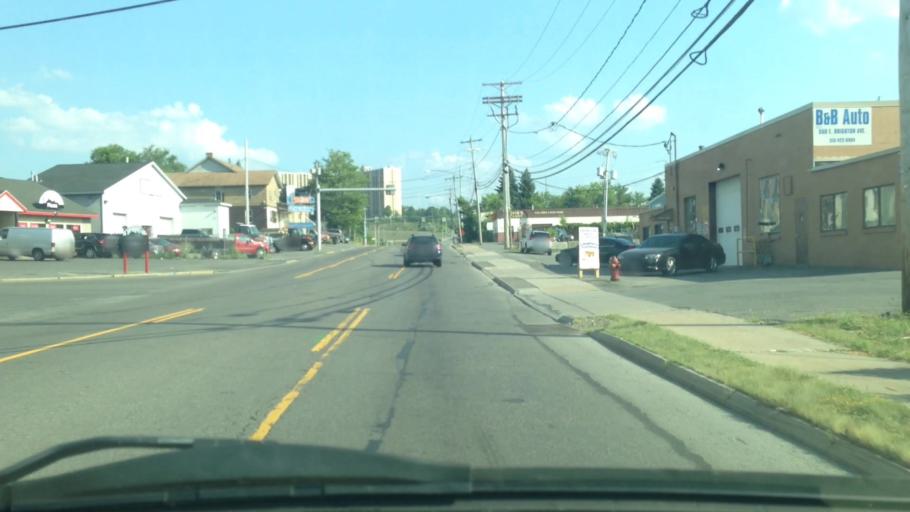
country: US
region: New York
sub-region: Onondaga County
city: Syracuse
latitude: 43.0129
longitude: -76.1349
